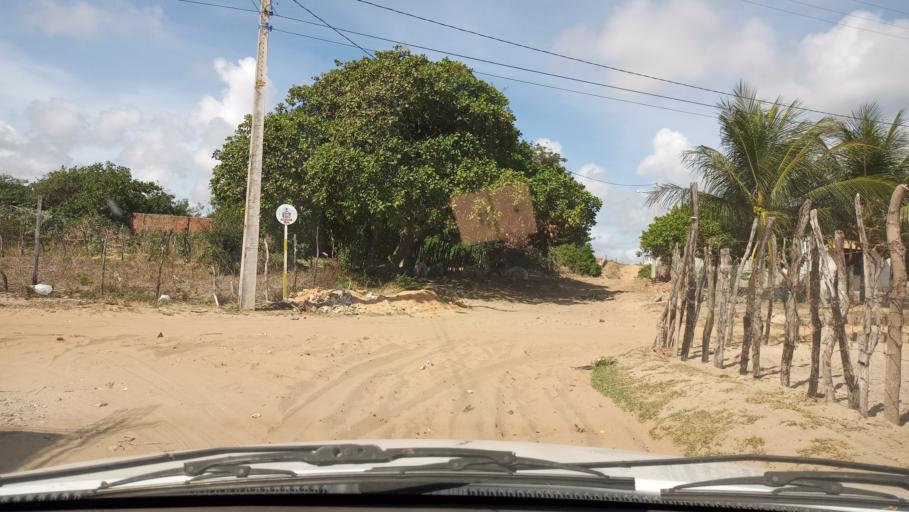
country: BR
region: Rio Grande do Norte
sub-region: Maxaranguape
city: Sao Miguel
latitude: -5.5148
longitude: -35.2656
